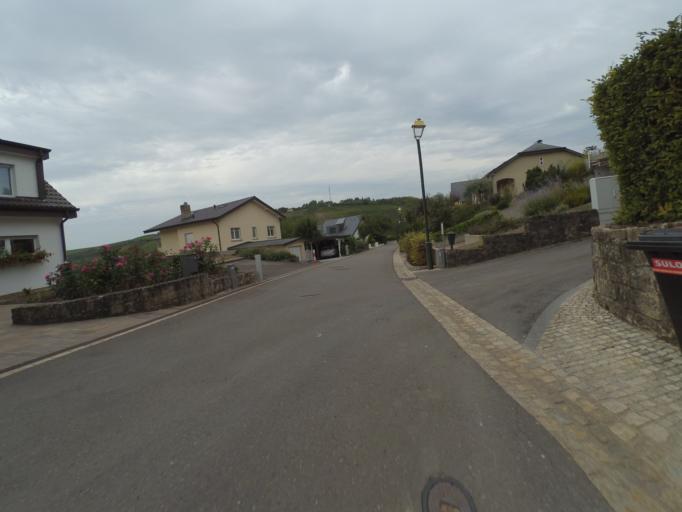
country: LU
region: Grevenmacher
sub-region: Canton de Grevenmacher
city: Wormeldange
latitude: 49.6018
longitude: 6.3899
